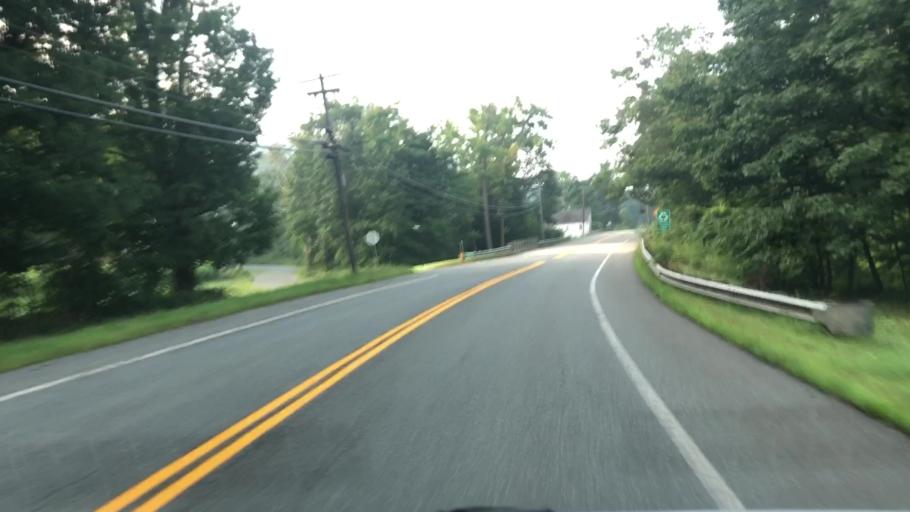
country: US
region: Massachusetts
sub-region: Franklin County
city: Buckland
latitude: 42.5685
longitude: -72.8016
